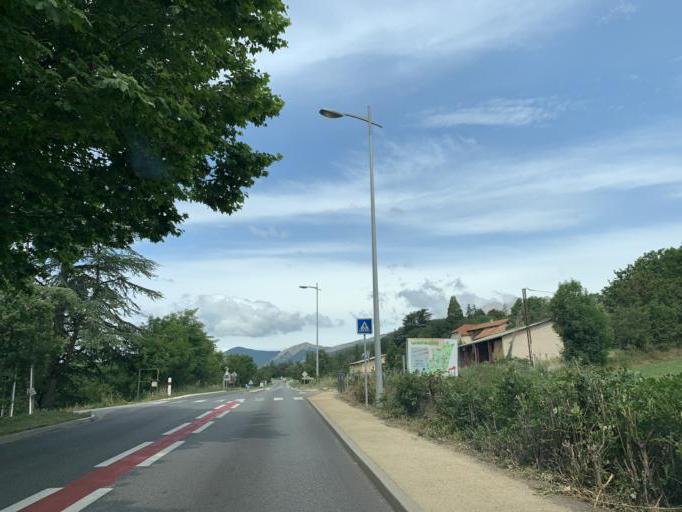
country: FR
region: Provence-Alpes-Cote d'Azur
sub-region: Departement des Hautes-Alpes
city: La Roche-des-Arnauds
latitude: 44.5421
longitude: 6.0120
